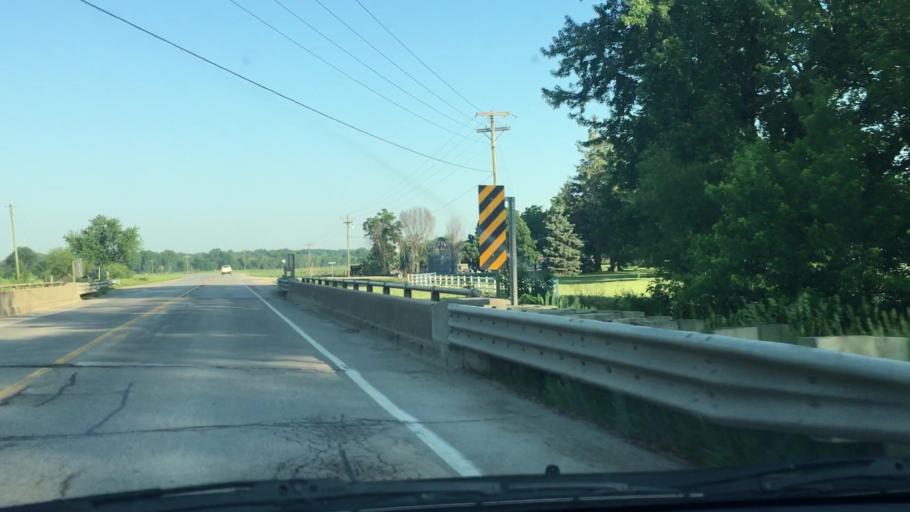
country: US
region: Iowa
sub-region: Johnson County
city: Tiffin
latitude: 41.7123
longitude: -91.6993
